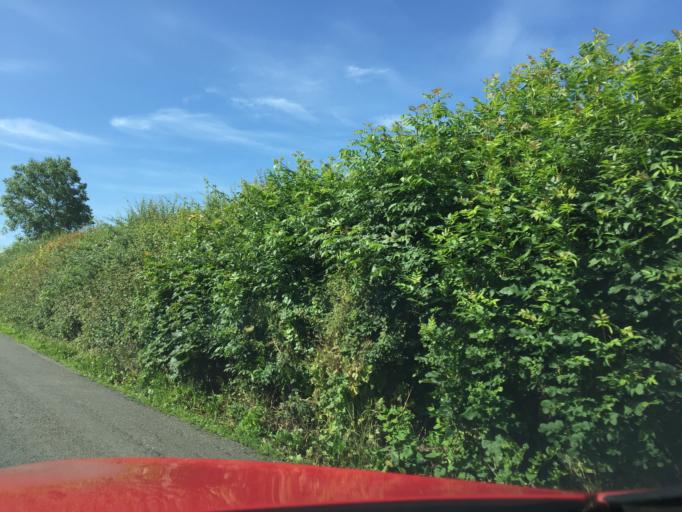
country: GB
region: England
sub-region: Gloucestershire
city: Stonehouse
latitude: 51.8146
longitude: -2.3287
